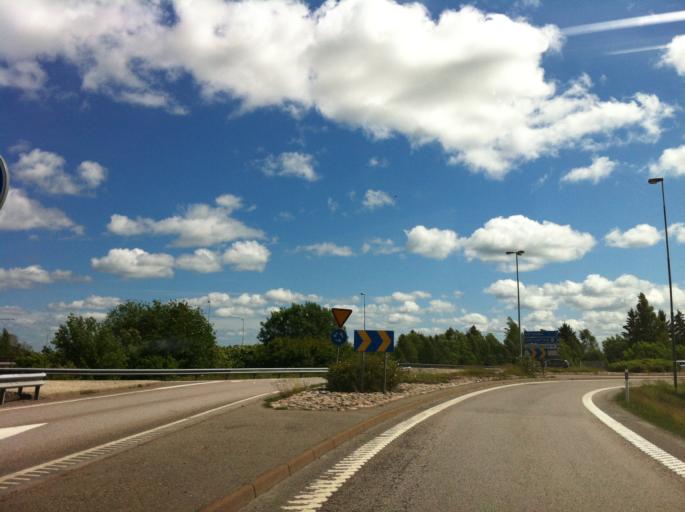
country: SE
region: Vaestra Goetaland
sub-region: Trollhattan
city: Trollhattan
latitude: 58.3011
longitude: 12.3284
